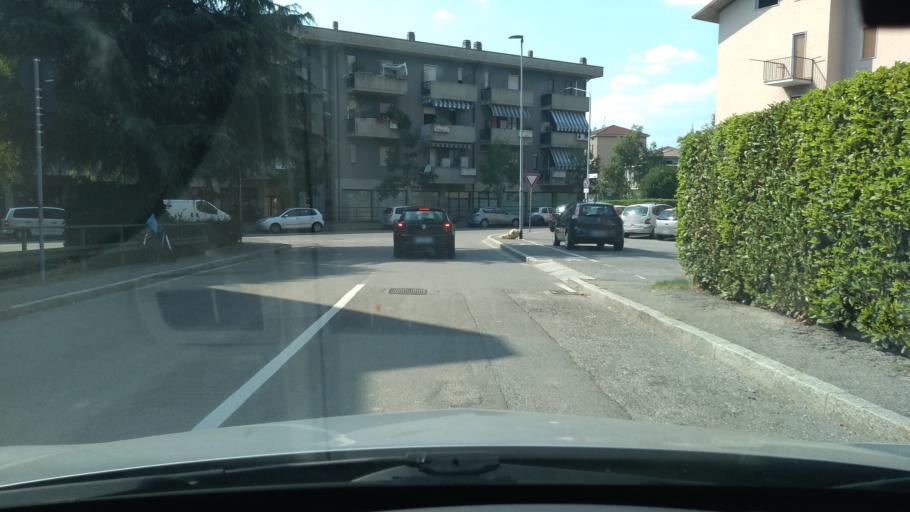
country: IT
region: Lombardy
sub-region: Provincia di Bergamo
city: Lallio
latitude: 45.6678
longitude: 9.6401
